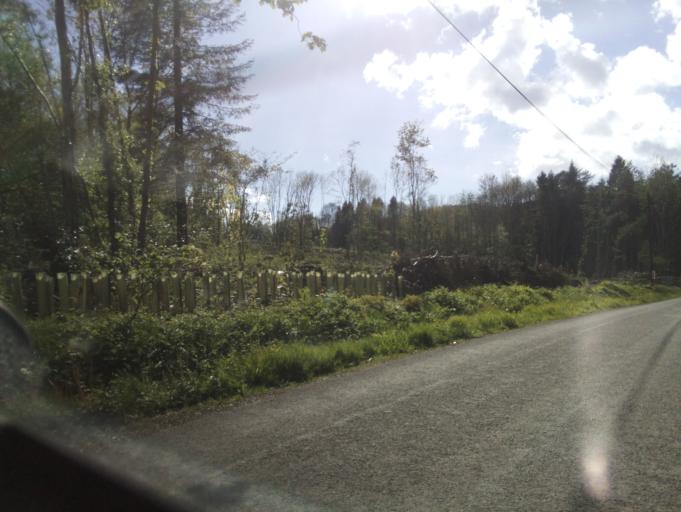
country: GB
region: Wales
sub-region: Caerphilly County Borough
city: Risca
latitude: 51.5761
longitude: -3.1099
